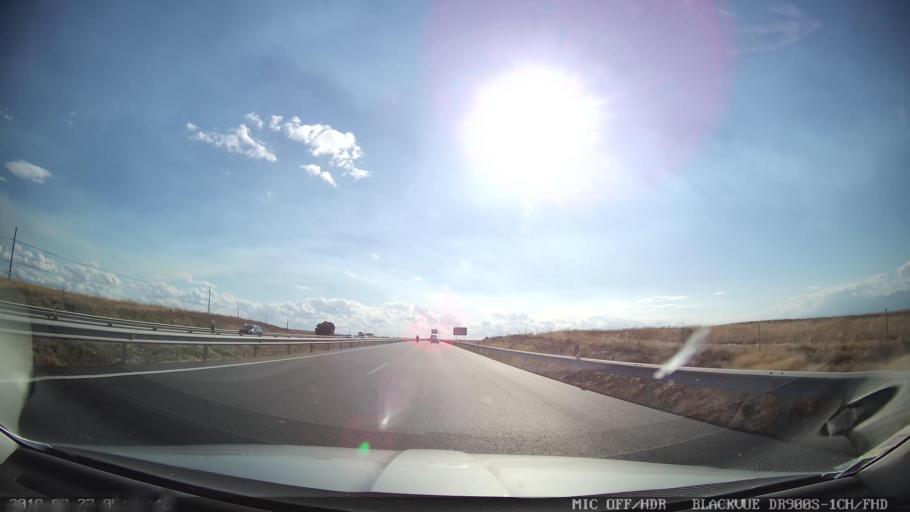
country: ES
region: Castille-La Mancha
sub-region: Province of Toledo
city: Herreruela de Oropesa
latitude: 39.9052
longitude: -5.2307
